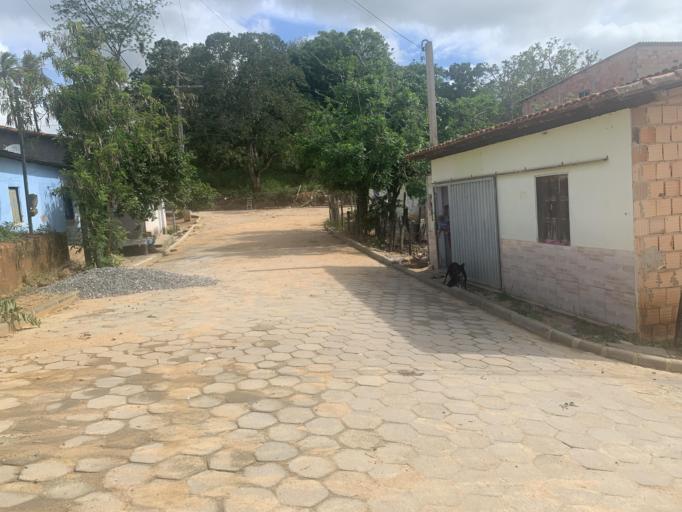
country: BR
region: Bahia
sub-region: Medeiros Neto
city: Medeiros Neto
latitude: -17.4353
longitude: -39.9354
